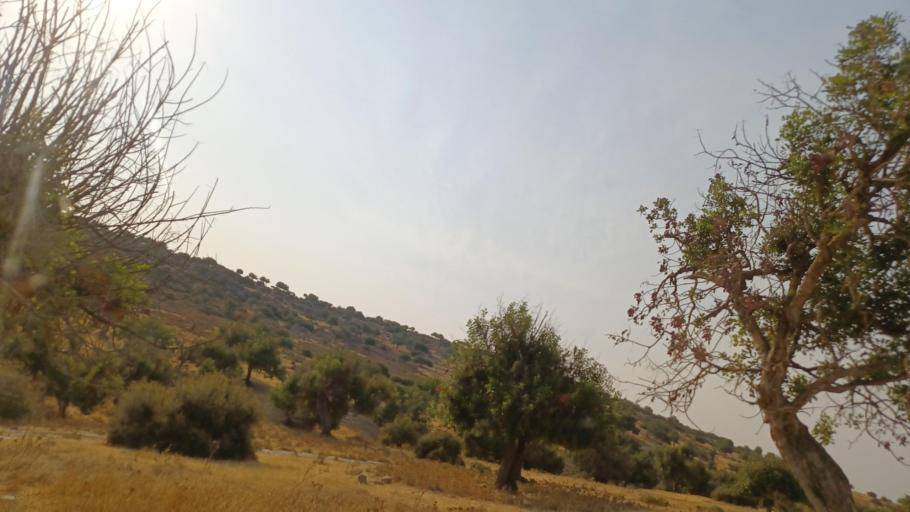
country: CY
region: Limassol
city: Pissouri
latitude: 34.6913
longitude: 32.6480
